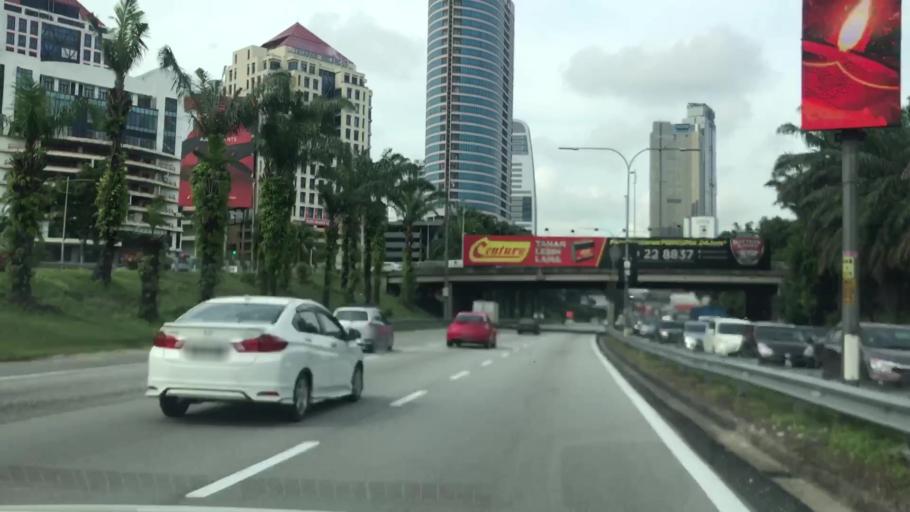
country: MY
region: Selangor
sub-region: Petaling
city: Petaling Jaya
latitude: 3.1069
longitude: 101.6478
